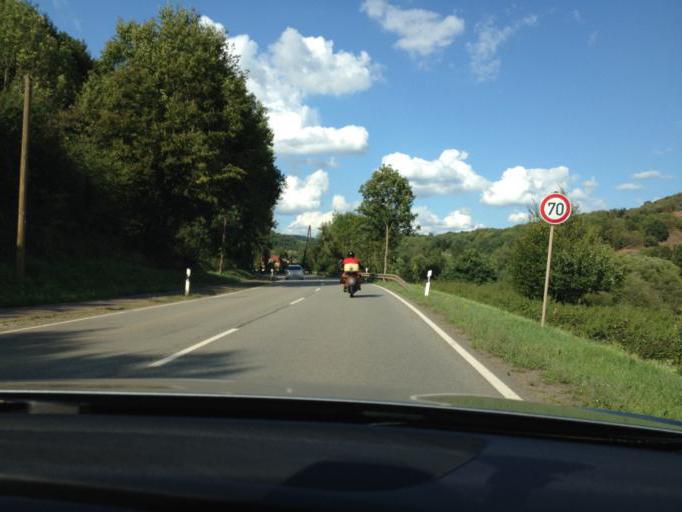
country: DE
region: Saarland
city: Schmelz
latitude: 49.4588
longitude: 6.8504
